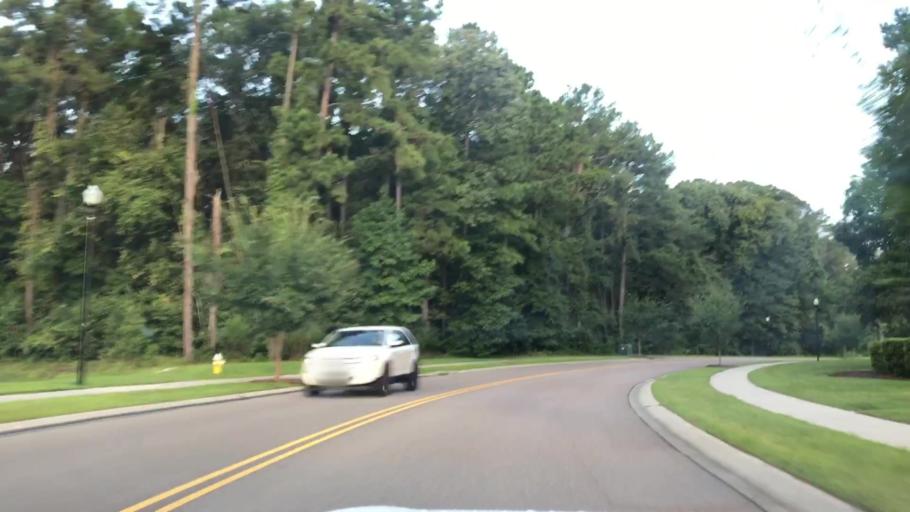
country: US
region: South Carolina
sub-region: Charleston County
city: Shell Point
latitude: 32.8246
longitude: -80.0943
